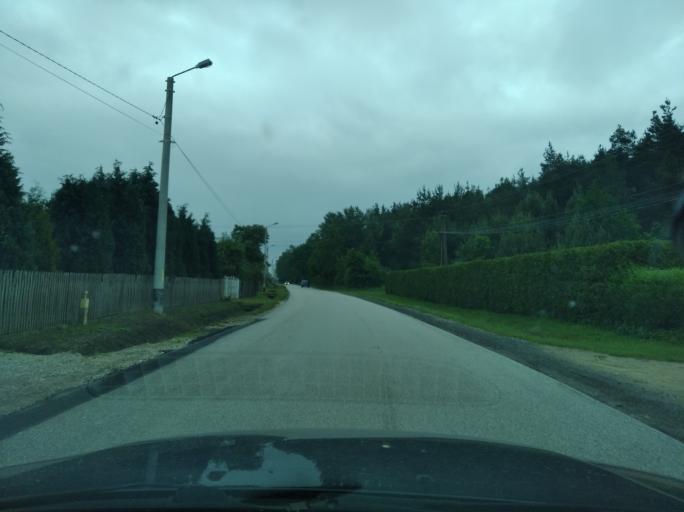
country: PL
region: Subcarpathian Voivodeship
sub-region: Powiat ropczycko-sedziszowski
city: Sedziszow Malopolski
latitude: 50.1128
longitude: 21.6735
